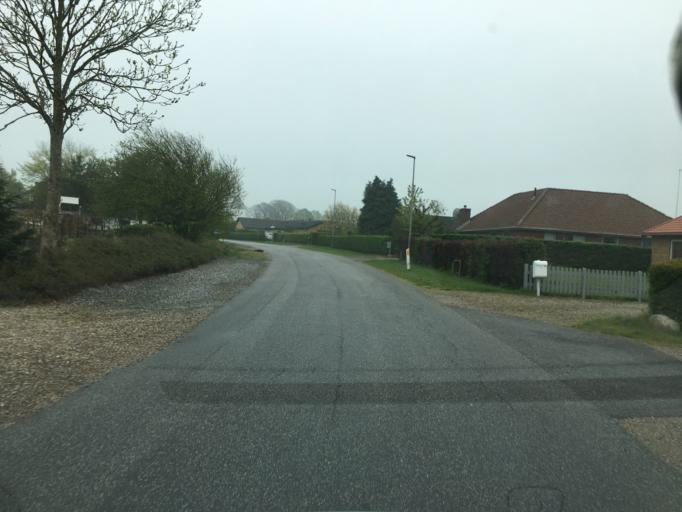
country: DK
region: South Denmark
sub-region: Haderslev Kommune
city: Haderslev
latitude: 55.2850
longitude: 9.4529
